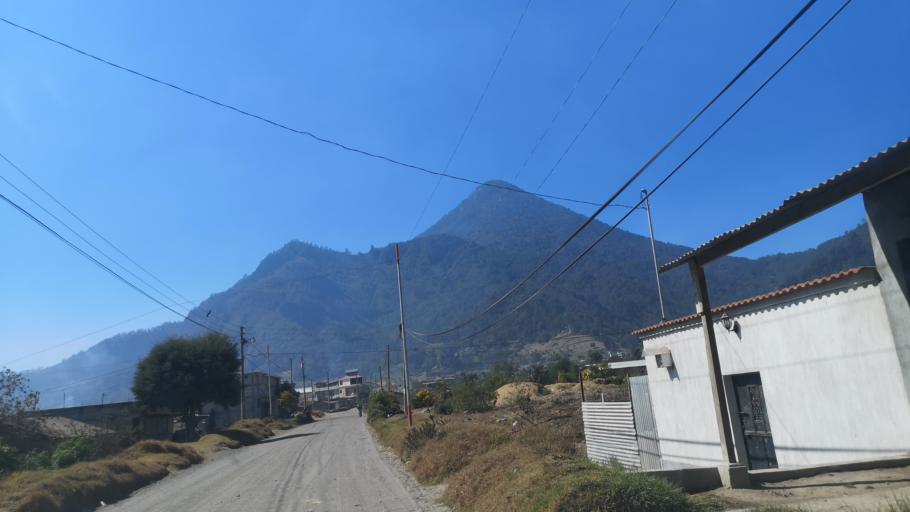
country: GT
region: Quetzaltenango
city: Quetzaltenango
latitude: 14.7942
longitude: -91.5436
